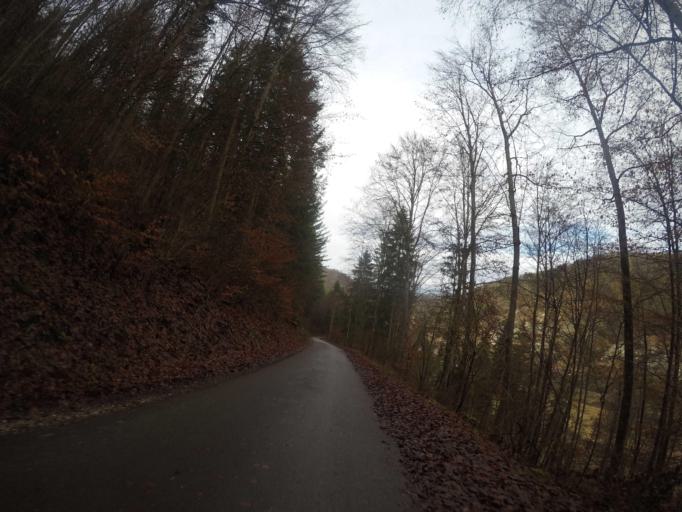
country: DE
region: Baden-Wuerttemberg
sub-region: Tuebingen Region
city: Dornstadt
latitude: 48.4420
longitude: 9.8690
